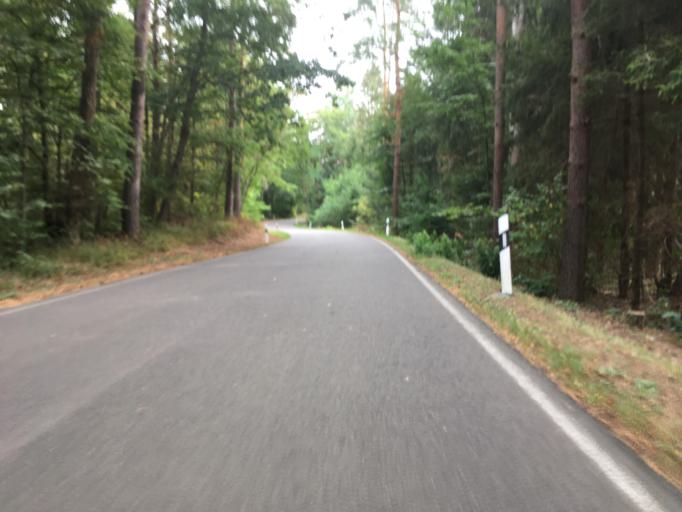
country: DE
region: Brandenburg
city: Milmersdorf
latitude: 53.1197
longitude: 13.6497
